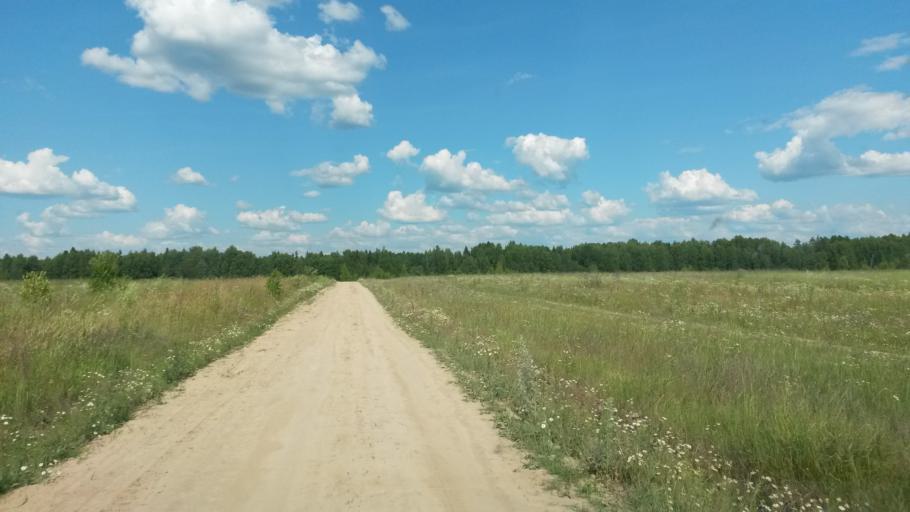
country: RU
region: Ivanovo
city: Zarechnyy
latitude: 57.4809
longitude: 42.3421
